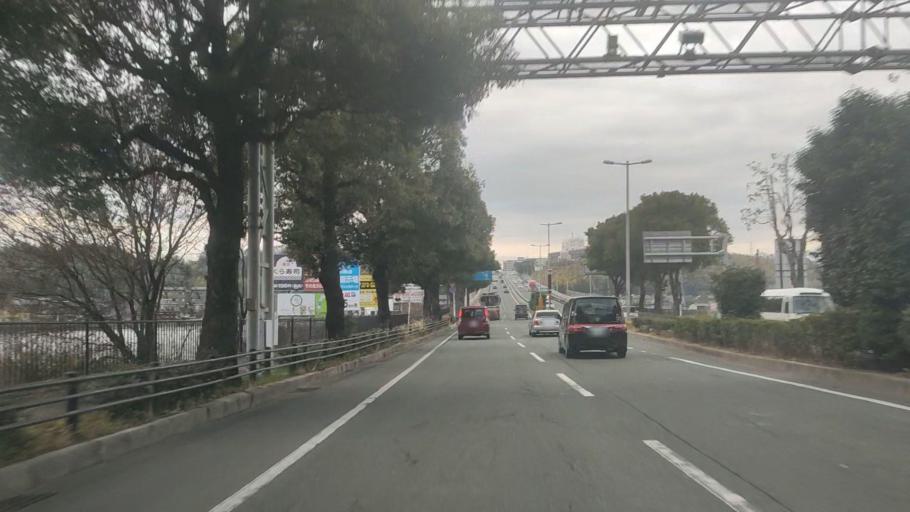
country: JP
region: Kumamoto
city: Ozu
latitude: 32.8455
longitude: 130.7814
